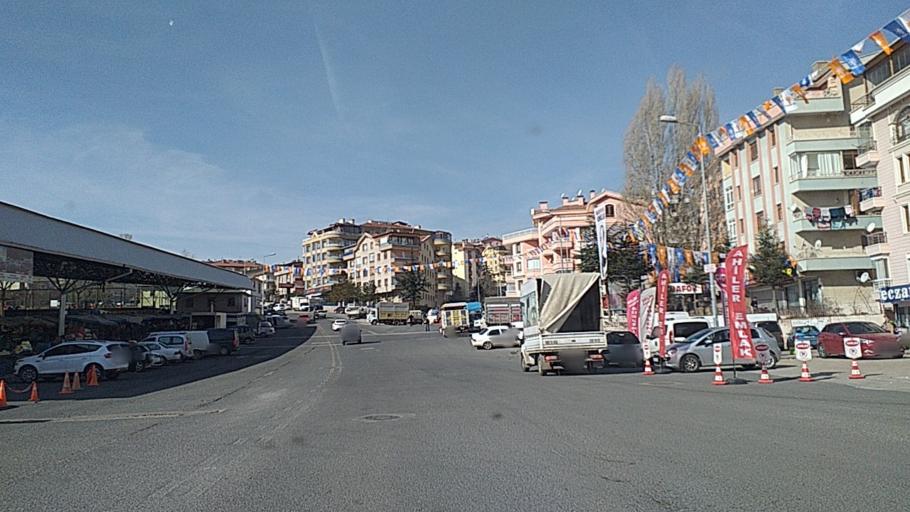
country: TR
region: Ankara
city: Ankara
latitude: 39.9880
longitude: 32.8192
